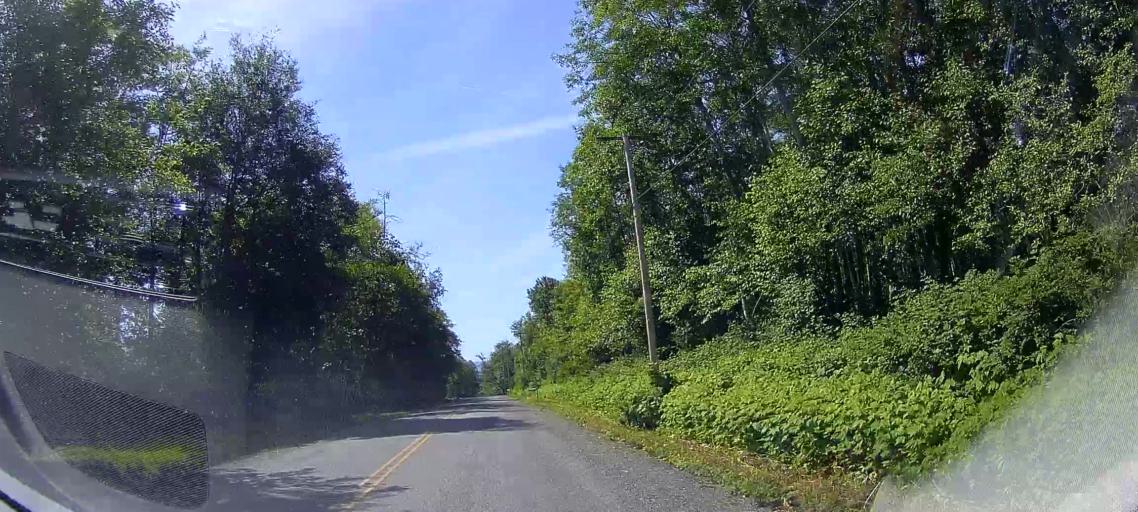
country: US
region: Washington
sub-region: Skagit County
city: Sedro-Woolley
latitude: 48.5307
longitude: -122.2481
